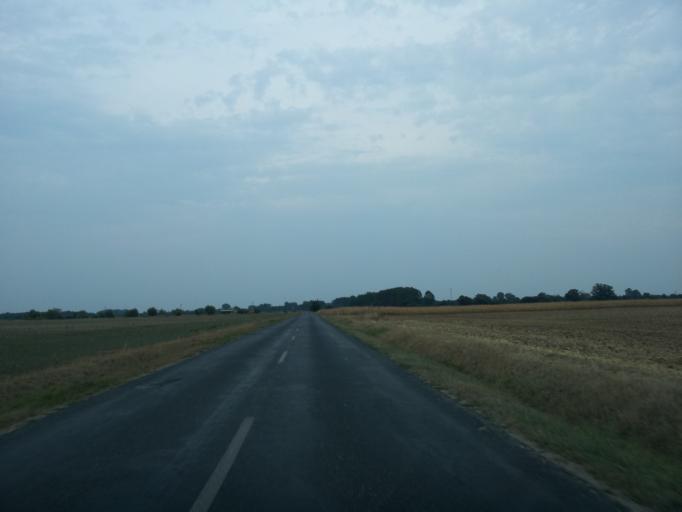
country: HU
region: Vas
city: Vep
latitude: 47.2047
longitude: 16.7987
